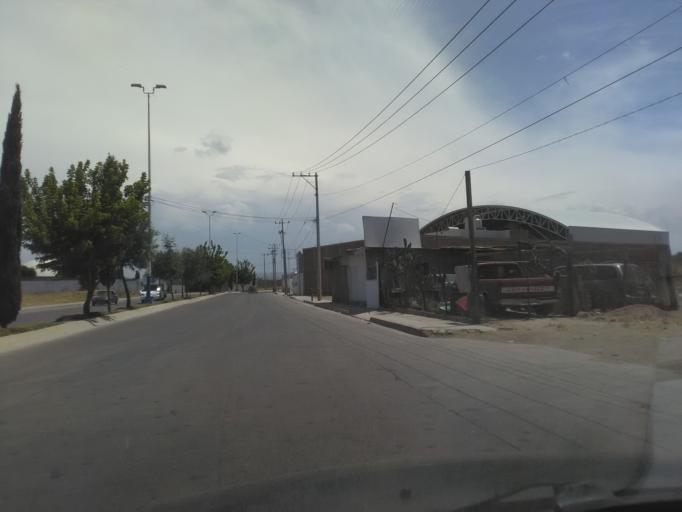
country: MX
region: Durango
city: Victoria de Durango
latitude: 24.0286
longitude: -104.6141
